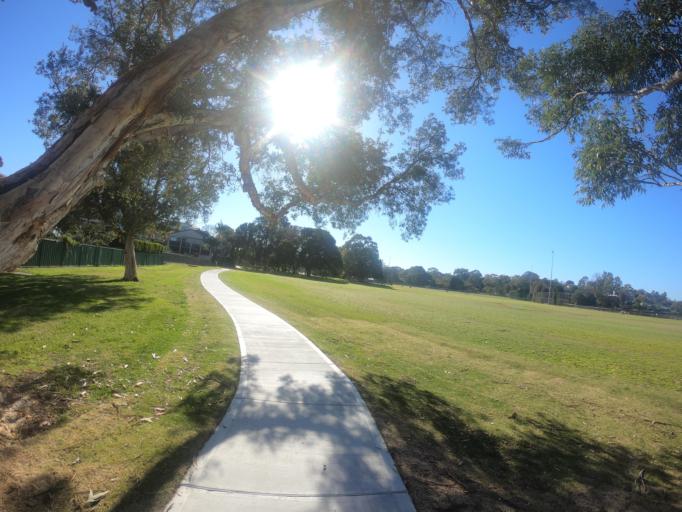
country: AU
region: New South Wales
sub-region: Canada Bay
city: Concord
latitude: -33.8291
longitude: 151.1106
